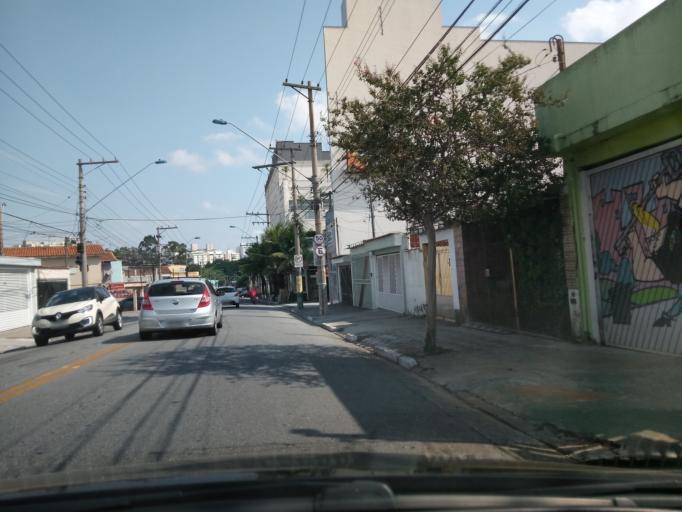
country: BR
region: Sao Paulo
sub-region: Sao Caetano Do Sul
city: Sao Caetano do Sul
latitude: -23.6447
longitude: -46.5748
